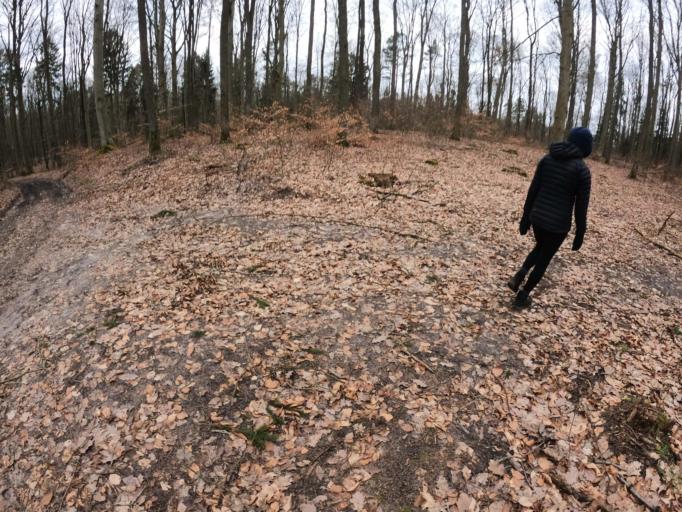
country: PL
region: West Pomeranian Voivodeship
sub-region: Powiat kamienski
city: Golczewo
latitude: 53.8083
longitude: 15.0131
